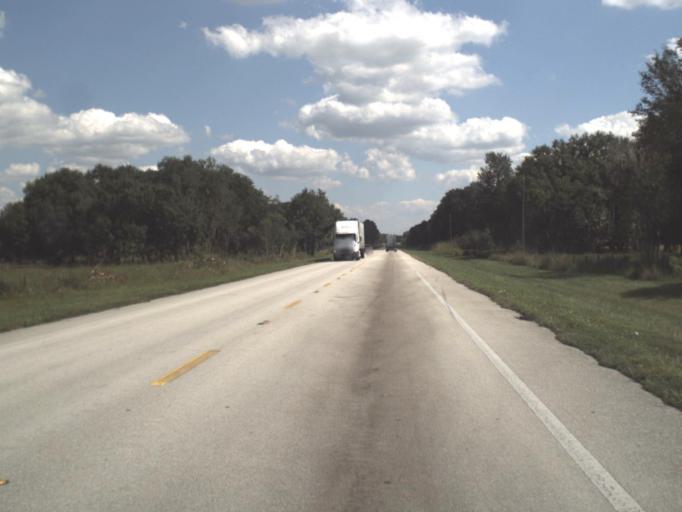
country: US
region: Florida
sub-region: Hardee County
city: Zolfo Springs
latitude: 27.4558
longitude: -81.6574
